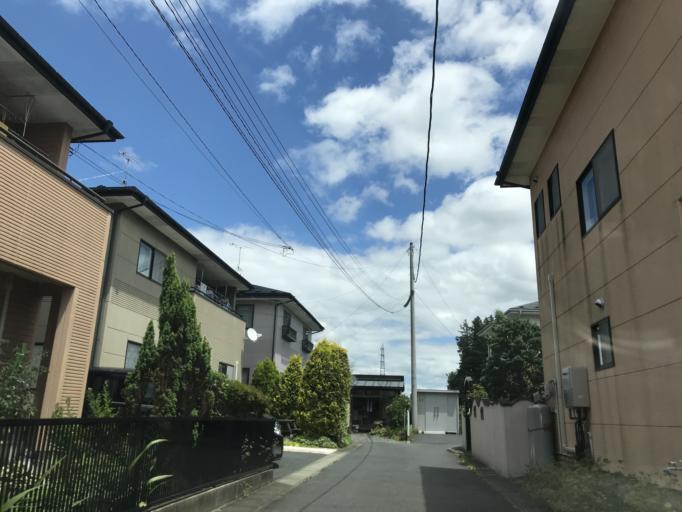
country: JP
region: Iwate
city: Ichinoseki
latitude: 38.9341
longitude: 141.0969
